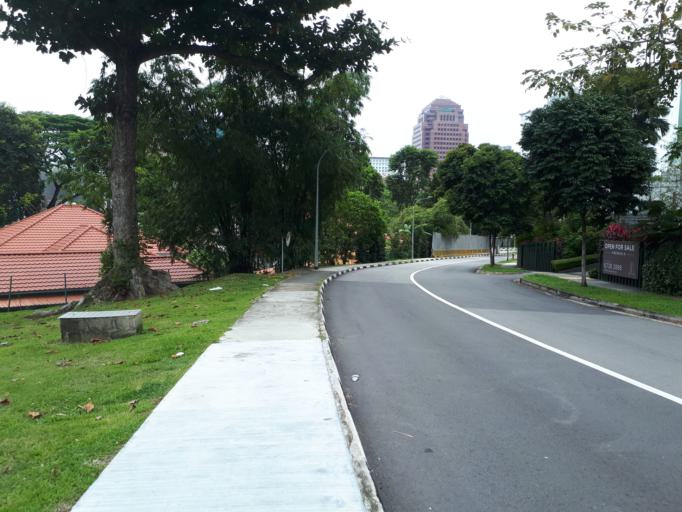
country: SG
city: Singapore
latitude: 1.2991
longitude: 103.8316
